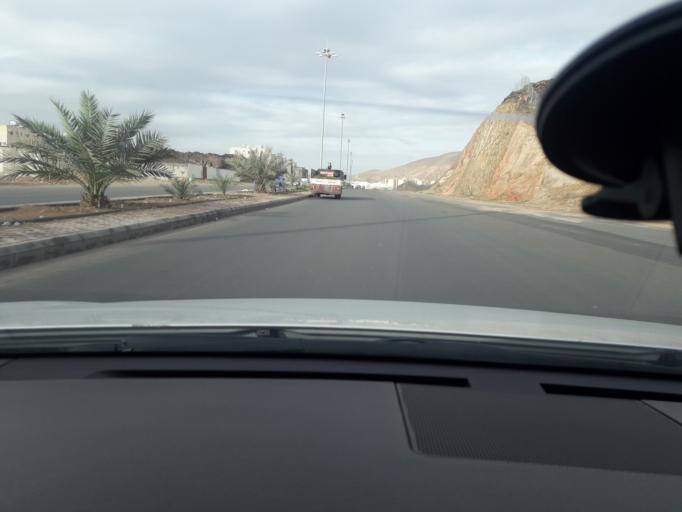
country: SA
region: Al Madinah al Munawwarah
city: Sultanah
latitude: 24.4676
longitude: 39.4994
